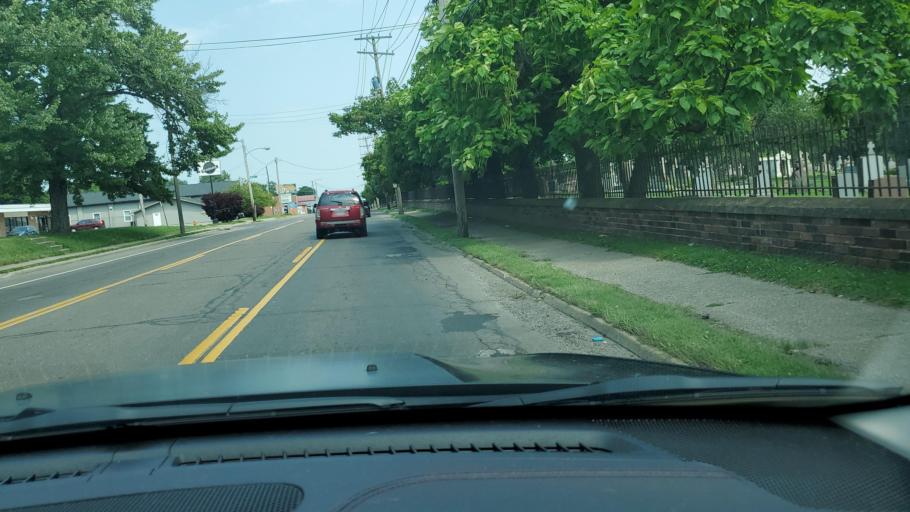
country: US
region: Ohio
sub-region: Mahoning County
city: Youngstown
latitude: 41.1026
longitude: -80.6920
